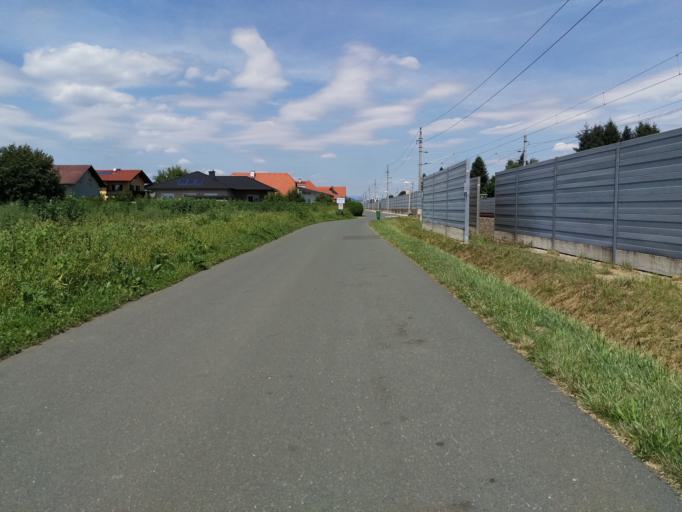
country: AT
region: Styria
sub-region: Politischer Bezirk Graz-Umgebung
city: Gossendorf
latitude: 46.9876
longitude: 15.4557
